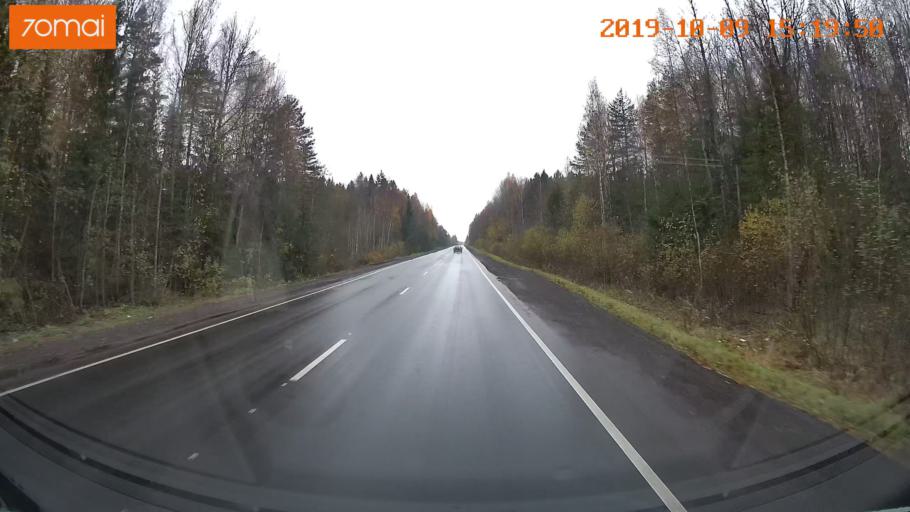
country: RU
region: Kostroma
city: Susanino
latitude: 58.0712
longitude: 41.5491
